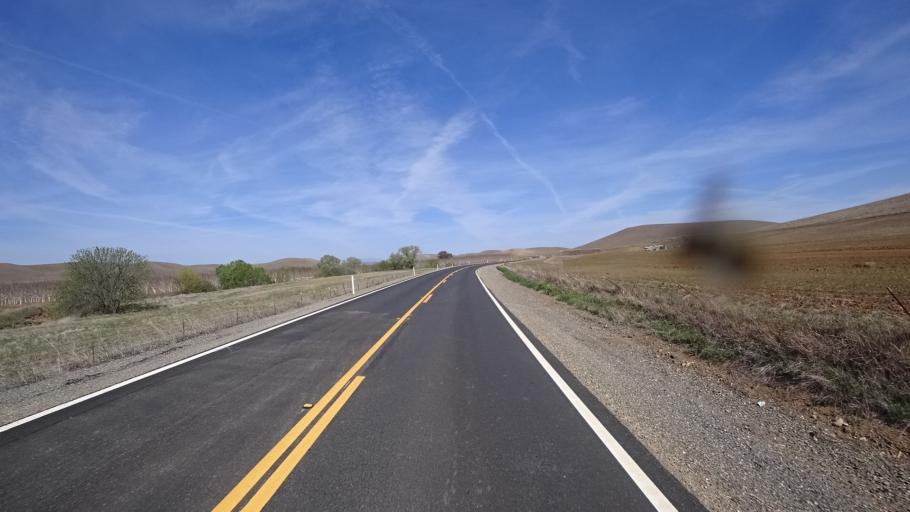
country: US
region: California
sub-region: Glenn County
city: Willows
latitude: 39.5353
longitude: -122.3431
